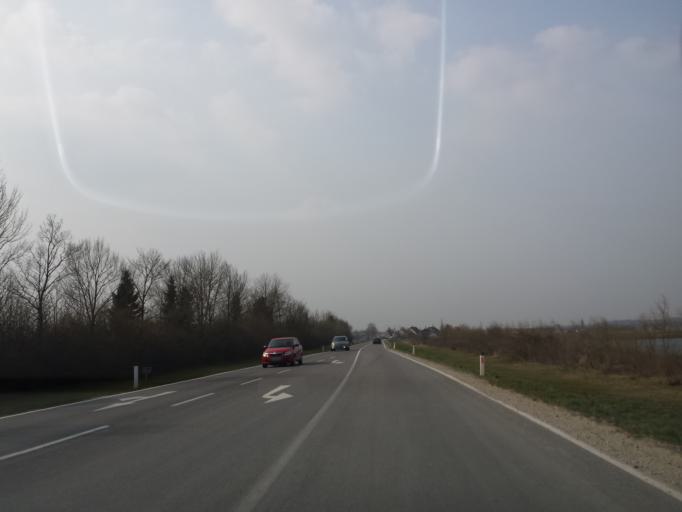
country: AT
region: Styria
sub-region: Politischer Bezirk Hartberg-Fuerstenfeld
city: Soechau
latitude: 47.0717
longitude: 16.0070
